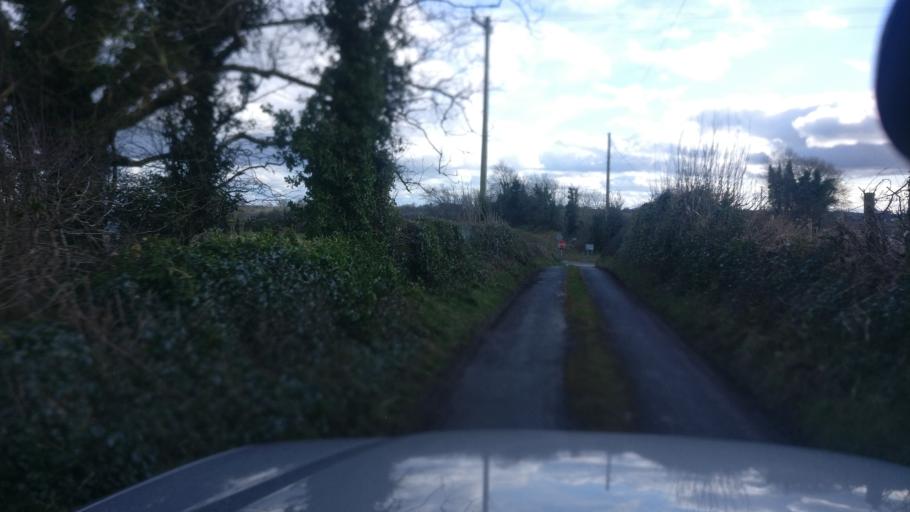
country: IE
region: Connaught
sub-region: County Galway
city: Loughrea
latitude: 53.2005
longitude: -8.4309
